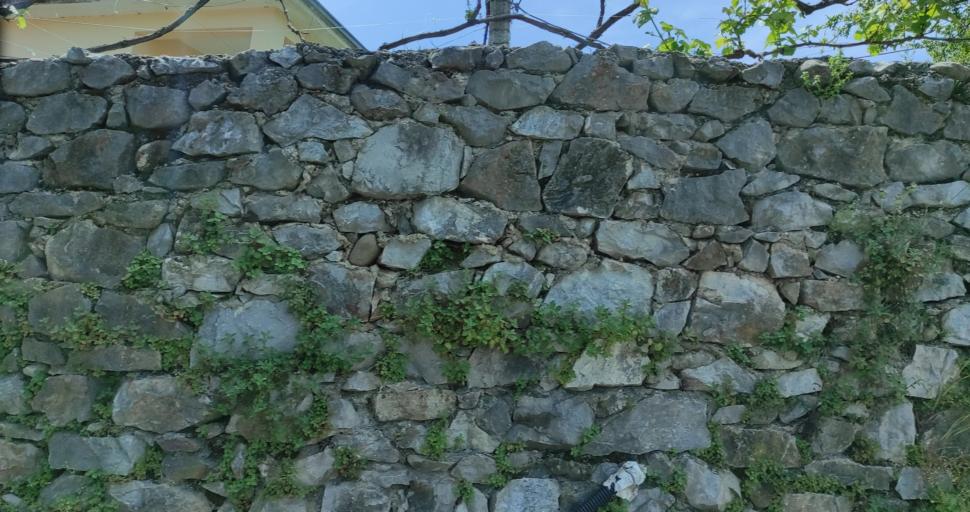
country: AL
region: Shkoder
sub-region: Rrethi i Shkodres
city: Guri i Zi
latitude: 42.1235
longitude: 19.5911
